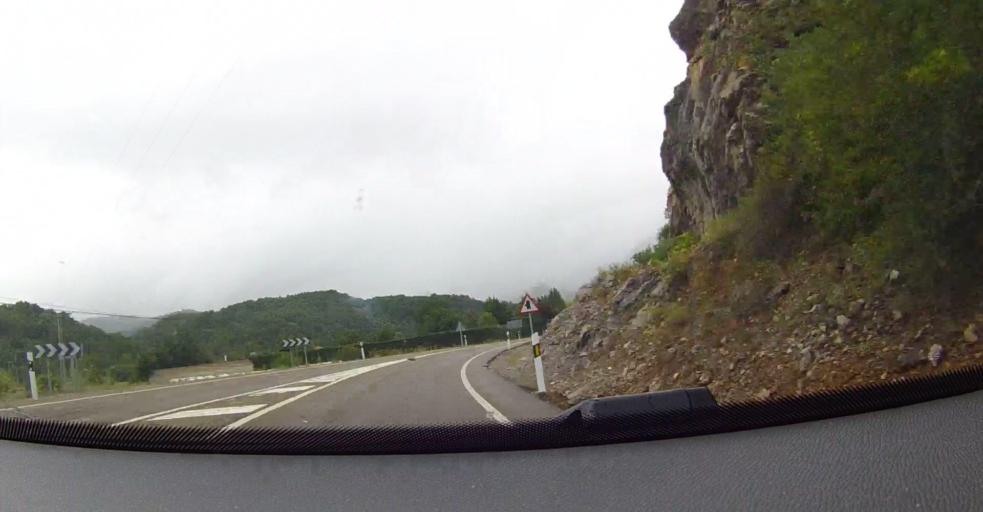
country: ES
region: Castille and Leon
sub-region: Provincia de Leon
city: Sabero
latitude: 42.8308
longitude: -5.1277
